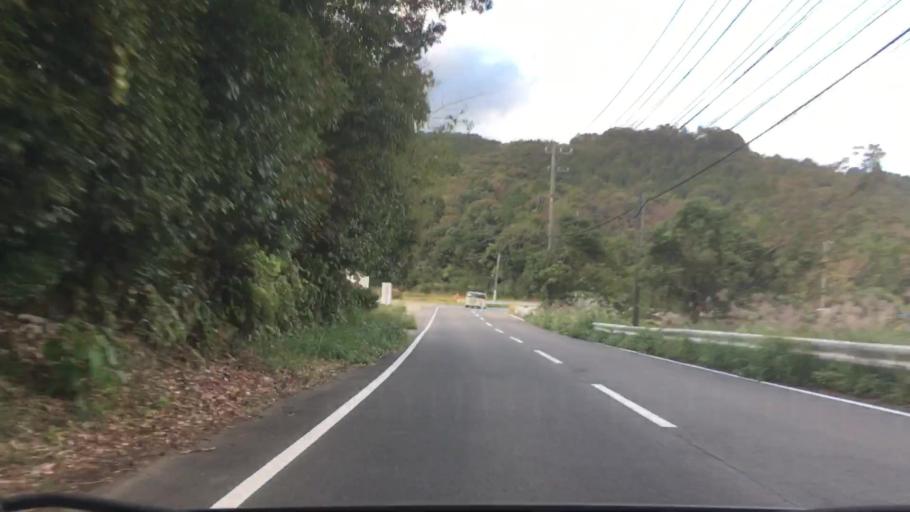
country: JP
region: Nagasaki
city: Sasebo
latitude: 32.9544
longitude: 129.6755
